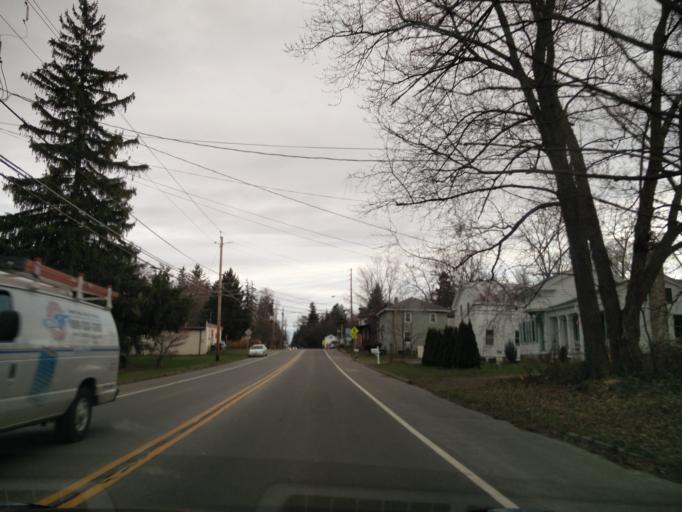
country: US
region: New York
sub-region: Tompkins County
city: Trumansburg
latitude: 42.5093
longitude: -76.6157
